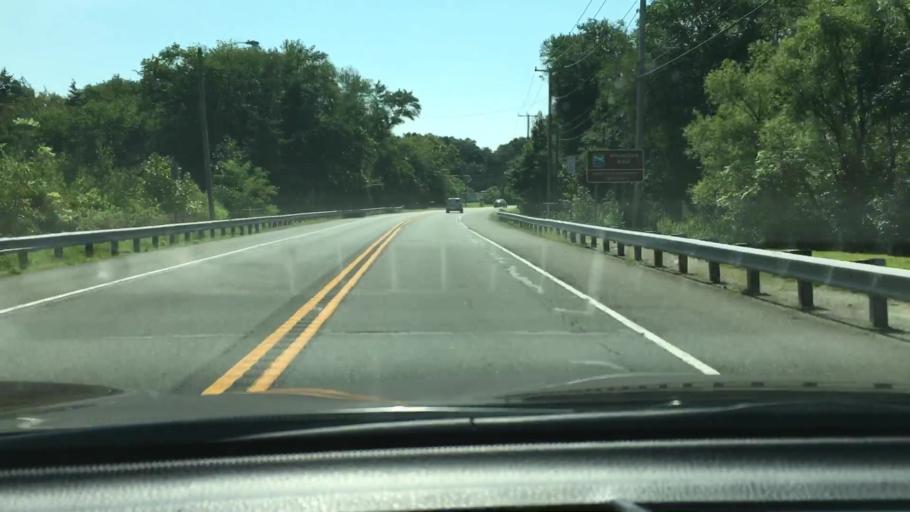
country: US
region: New Jersey
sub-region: Cumberland County
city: Laurel Lake
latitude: 39.3734
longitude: -74.9453
